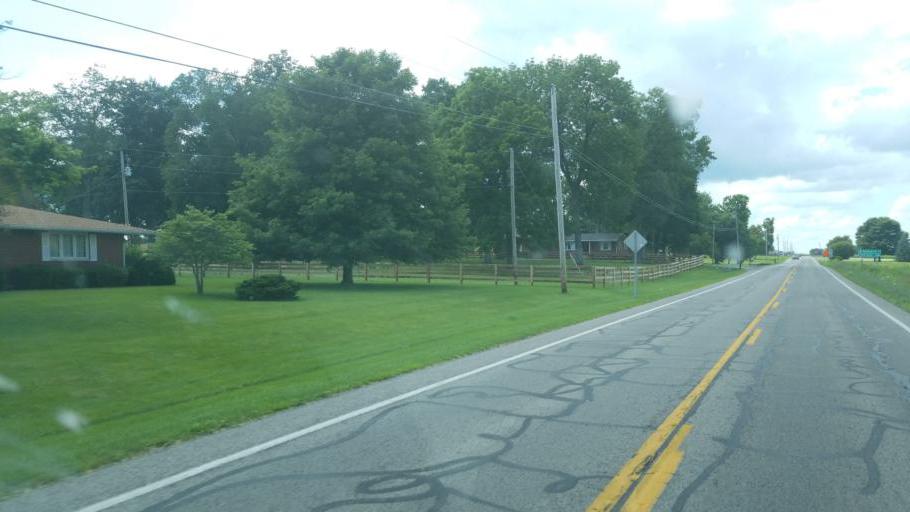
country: US
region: Ohio
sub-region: Highland County
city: Greenfield
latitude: 39.3766
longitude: -83.3806
